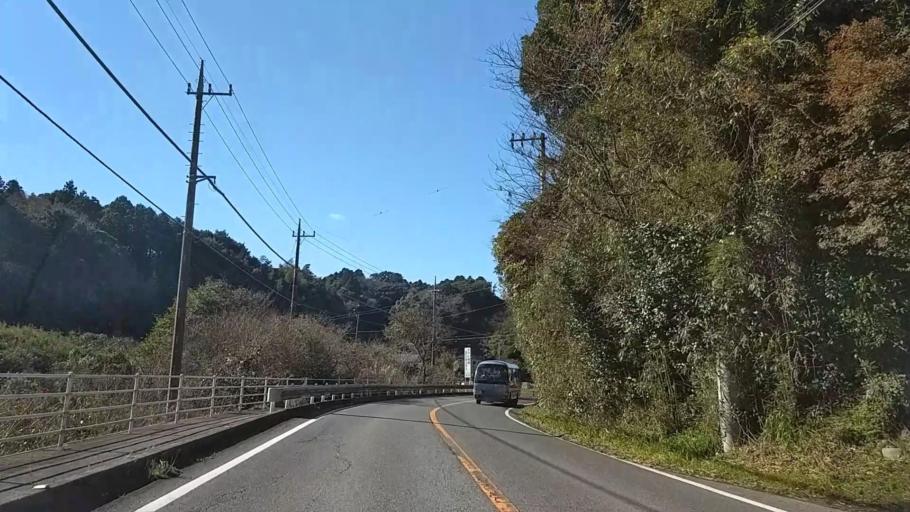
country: JP
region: Chiba
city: Tateyama
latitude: 34.9546
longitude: 139.8473
